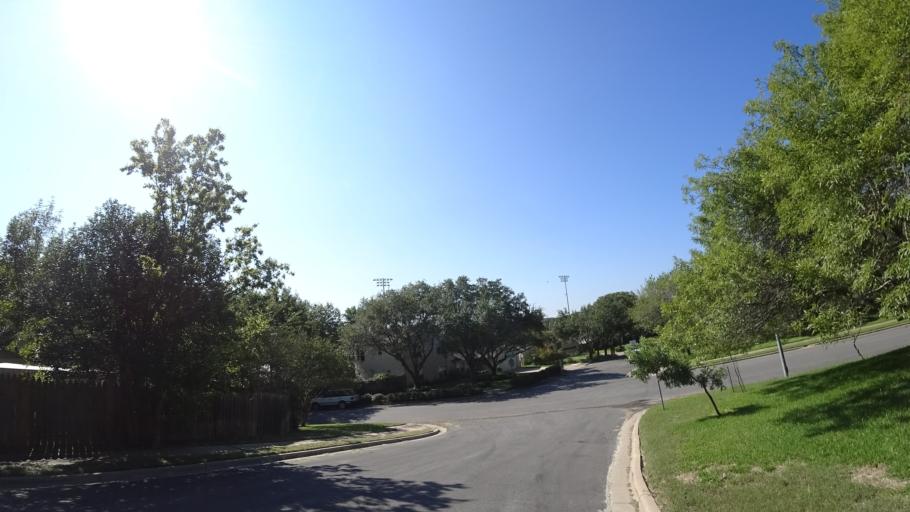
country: US
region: Texas
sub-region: Travis County
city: Rollingwood
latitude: 30.2733
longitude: -97.8037
